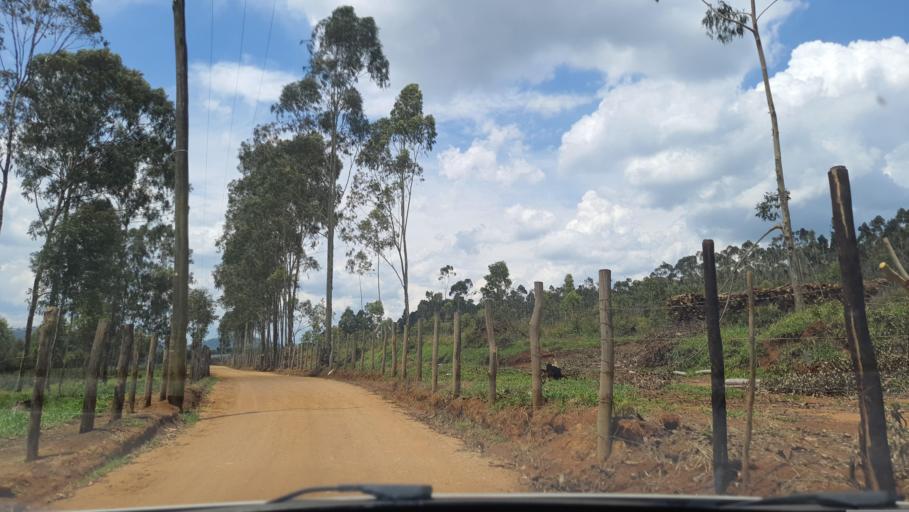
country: BR
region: Sao Paulo
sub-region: Bom Jesus Dos Perdoes
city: Bom Jesus dos Perdoes
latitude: -23.1534
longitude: -46.4636
